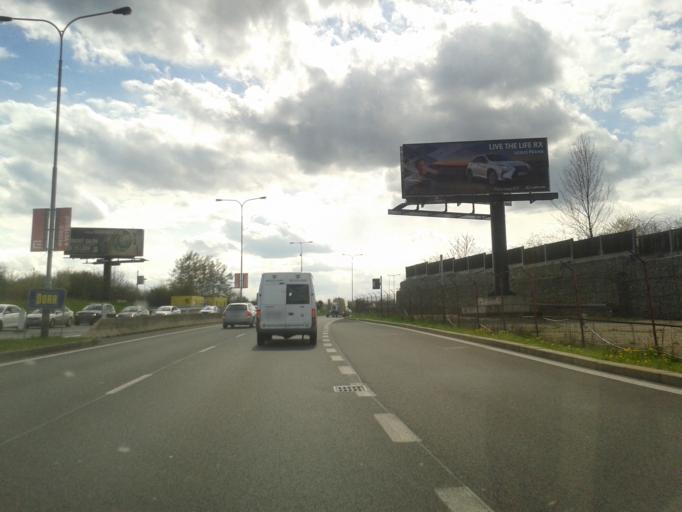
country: CZ
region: Praha
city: Branik
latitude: 50.0299
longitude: 14.3800
